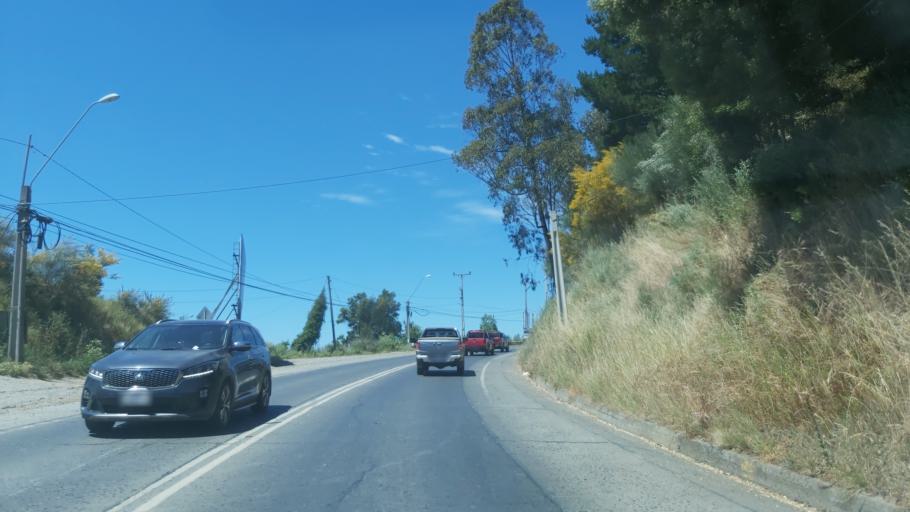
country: CL
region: Maule
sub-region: Provincia de Talca
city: Constitucion
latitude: -35.3501
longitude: -72.4107
